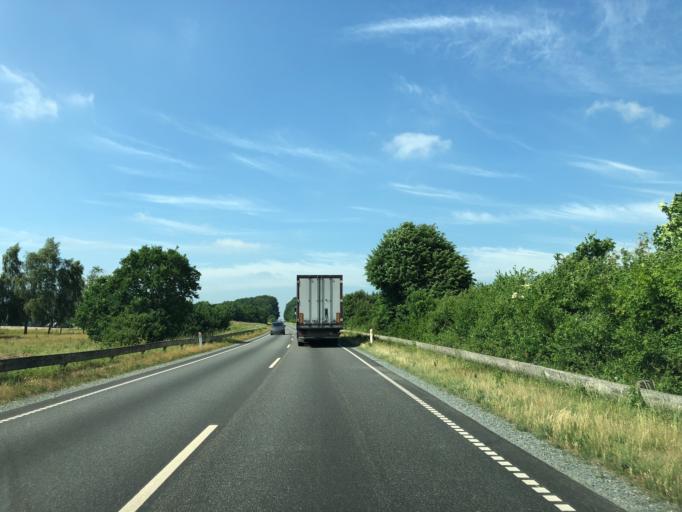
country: DK
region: South Denmark
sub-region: Kolding Kommune
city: Kolding
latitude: 55.6020
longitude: 9.4358
